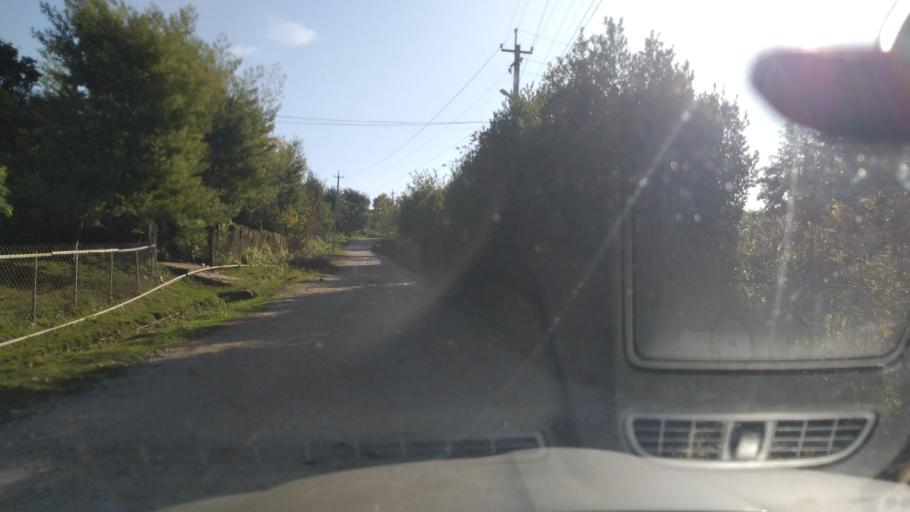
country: GE
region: Abkhazia
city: Stantsiya Novyy Afon
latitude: 43.0611
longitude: 40.8915
